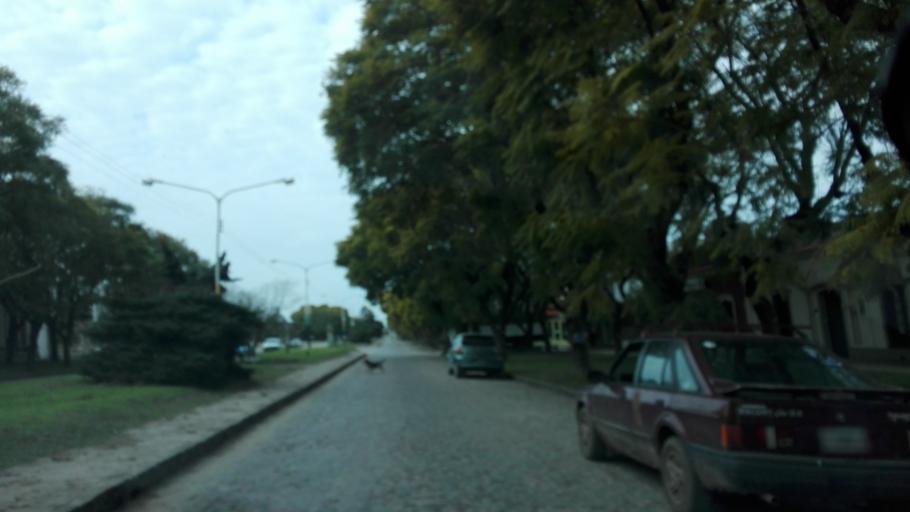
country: AR
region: Buenos Aires
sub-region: Partido de Chascomus
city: Chascomus
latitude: -35.5777
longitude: -58.0136
